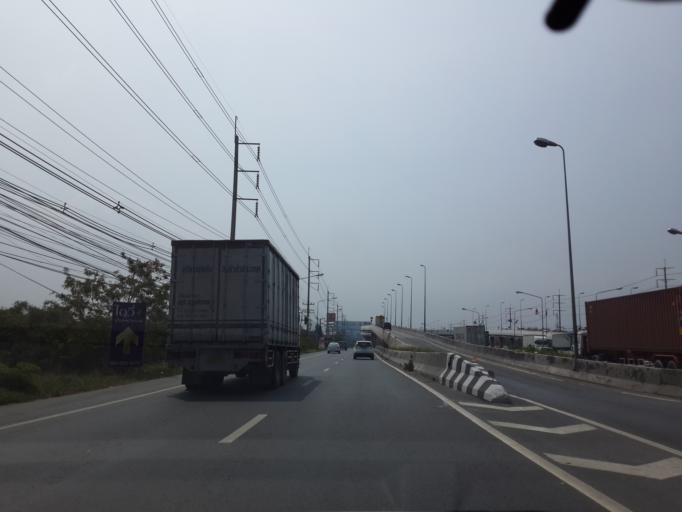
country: TH
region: Chon Buri
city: Chon Buri
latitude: 13.4371
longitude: 101.0016
